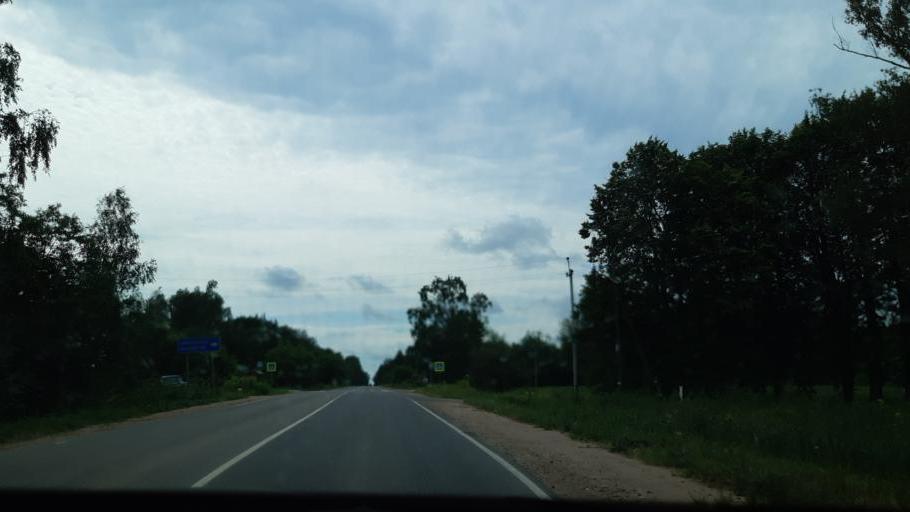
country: RU
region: Moskovskaya
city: Vereya
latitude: 55.3824
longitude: 36.2939
